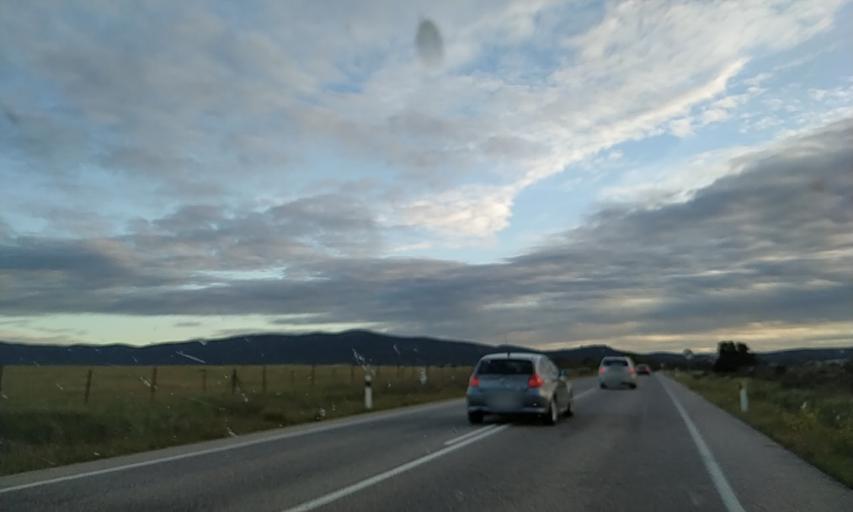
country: ES
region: Extremadura
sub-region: Provincia de Caceres
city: Malpartida de Caceres
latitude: 39.3372
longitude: -6.4809
